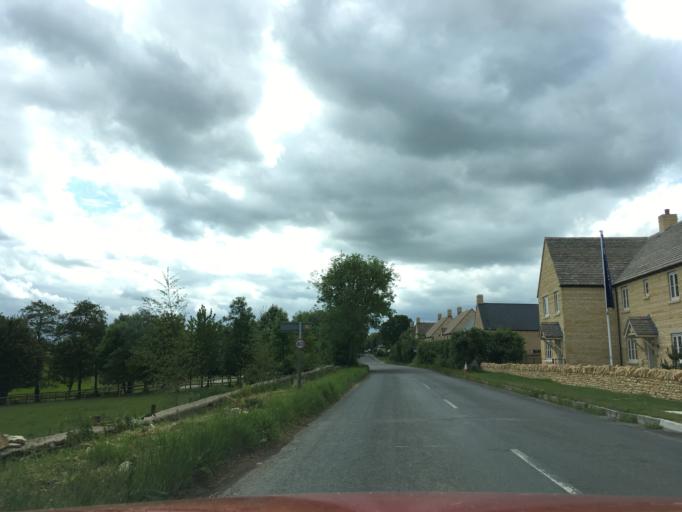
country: GB
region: England
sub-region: Gloucestershire
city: Tetbury
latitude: 51.6450
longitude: -2.1457
